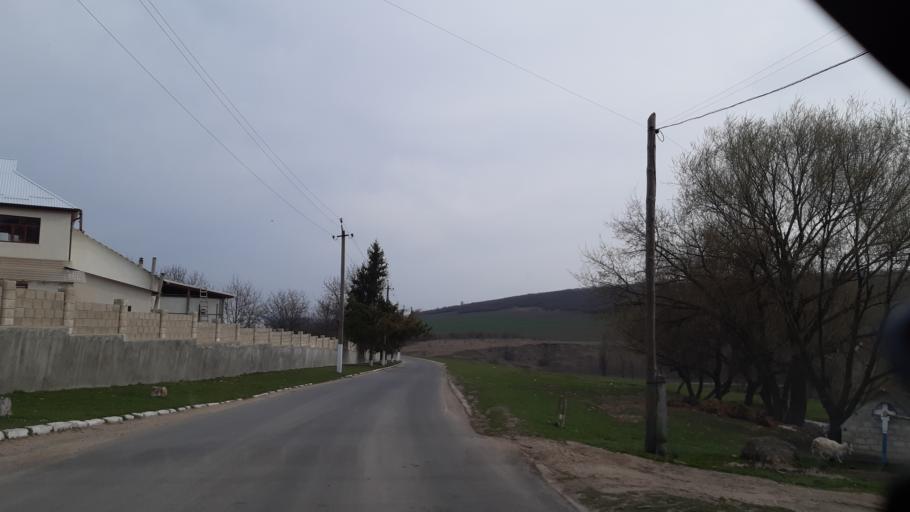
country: MD
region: Soldanesti
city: Soldanesti
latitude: 47.6824
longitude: 28.7810
